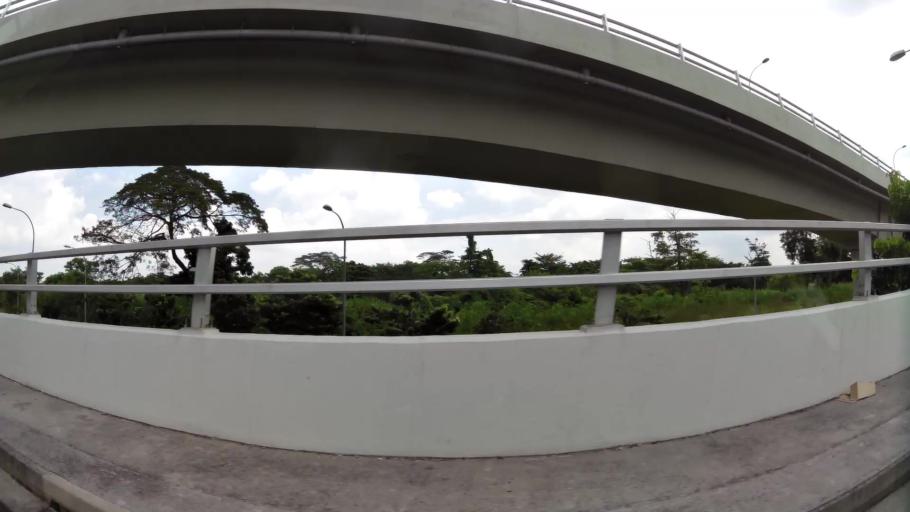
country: MY
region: Johor
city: Kampung Pasir Gudang Baru
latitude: 1.3965
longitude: 103.8575
